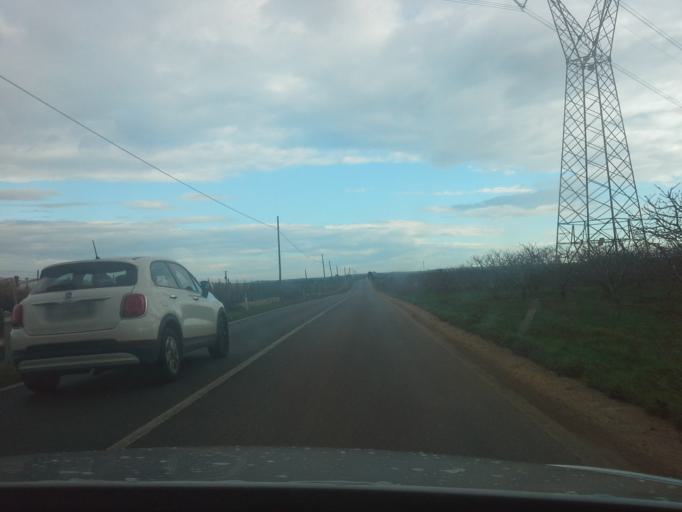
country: IT
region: Apulia
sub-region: Provincia di Bari
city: Casamassima
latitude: 40.9399
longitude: 16.9604
